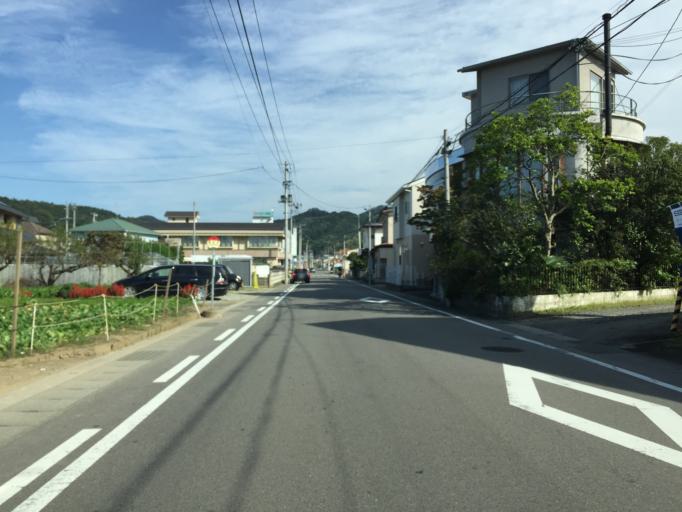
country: JP
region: Fukushima
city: Fukushima-shi
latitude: 37.7475
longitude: 140.4797
